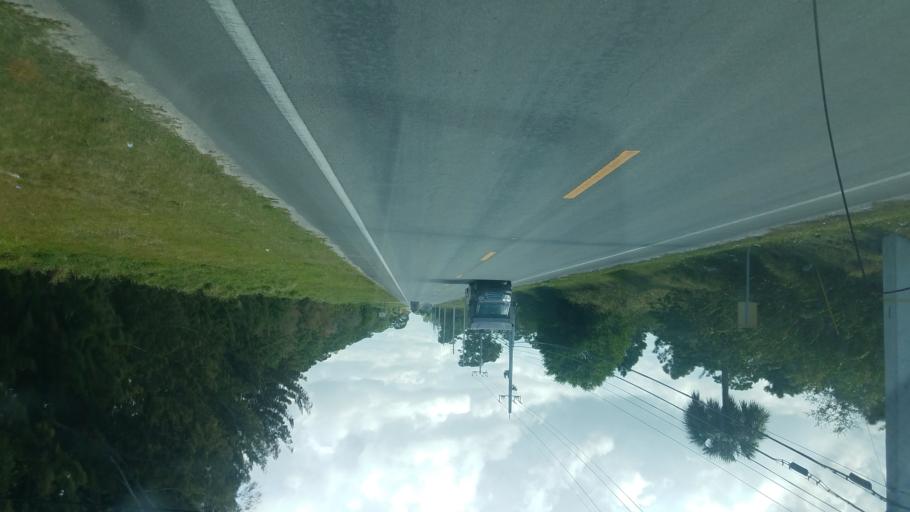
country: US
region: Florida
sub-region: Saint Lucie County
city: Lakewood Park
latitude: 27.4475
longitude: -80.4117
